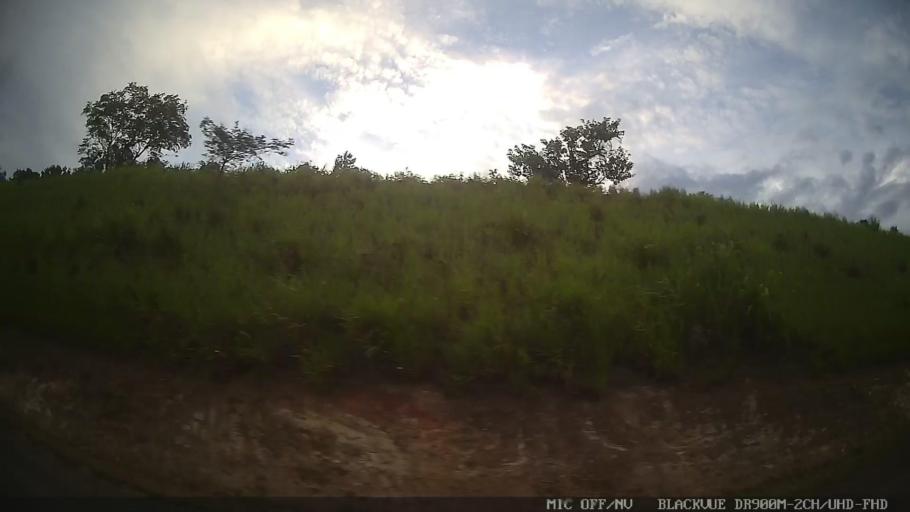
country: BR
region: Sao Paulo
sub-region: Itu
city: Itu
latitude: -23.2601
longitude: -47.2708
